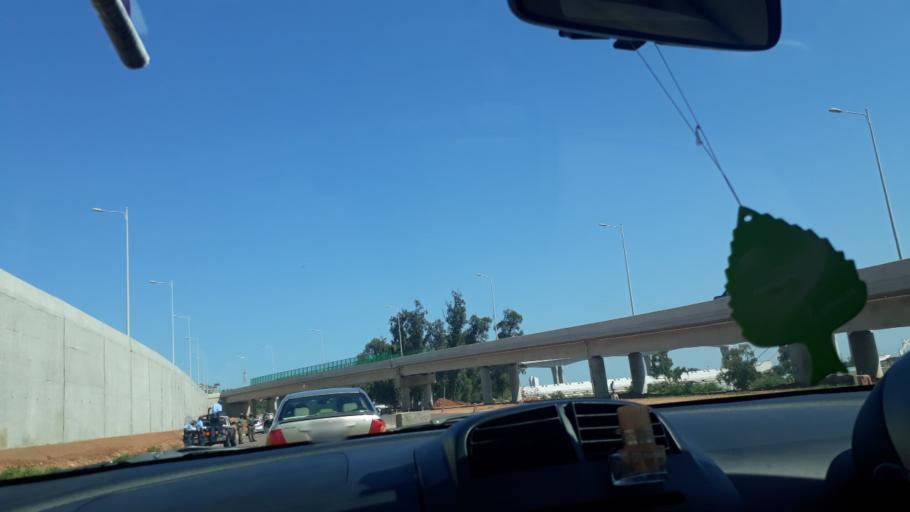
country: MZ
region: Maputo City
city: Maputo
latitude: -25.9588
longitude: 32.5562
